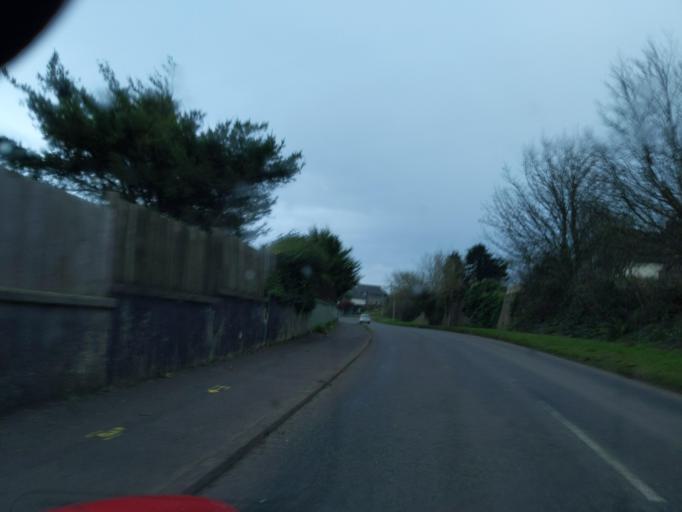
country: GB
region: England
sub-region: Devon
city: Wembury
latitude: 50.3368
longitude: -4.0729
